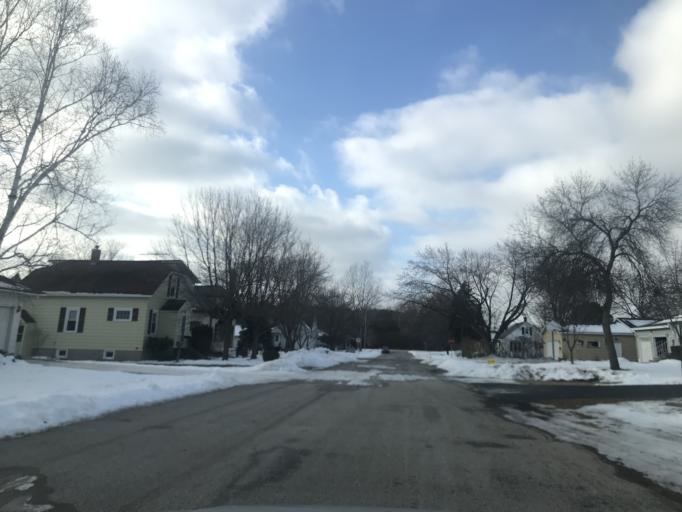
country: US
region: Wisconsin
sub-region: Marinette County
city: Marinette
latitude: 45.1011
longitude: -87.6479
